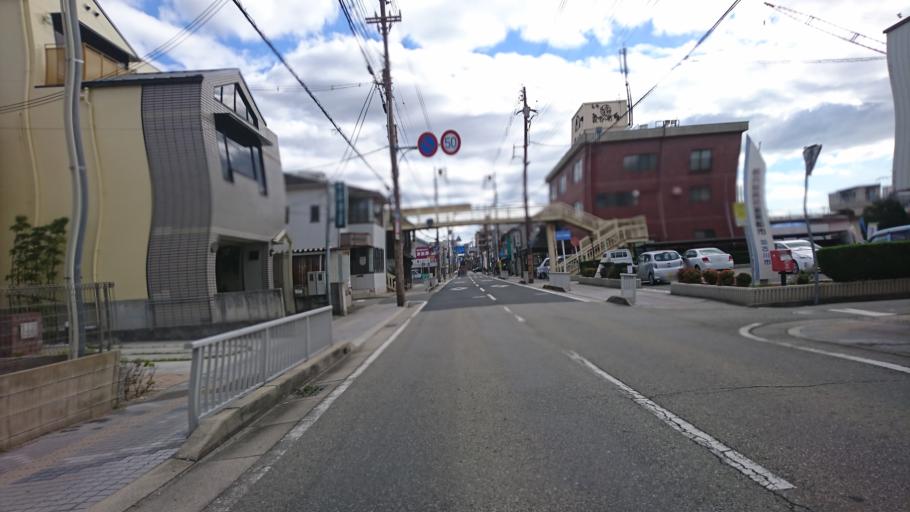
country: JP
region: Hyogo
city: Kakogawacho-honmachi
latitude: 34.7675
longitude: 134.8332
